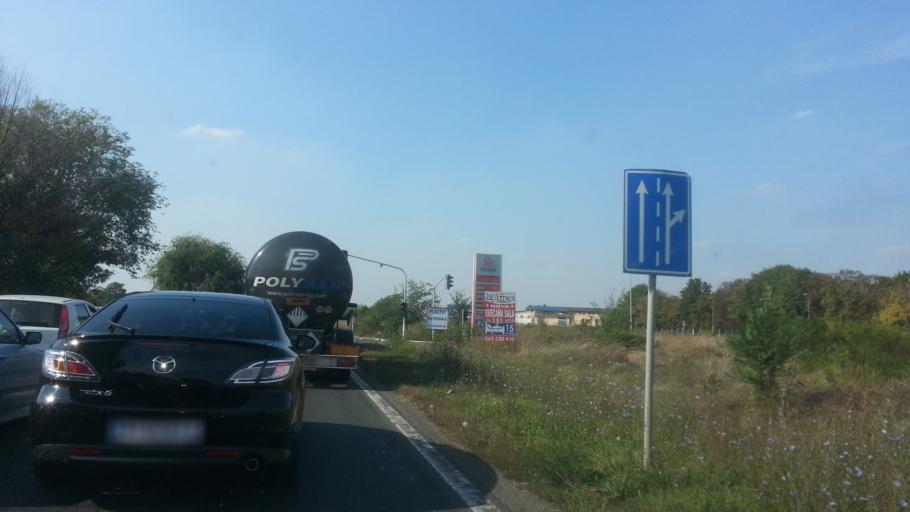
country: RS
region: Central Serbia
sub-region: Belgrade
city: Zemun
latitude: 44.8744
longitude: 20.3310
